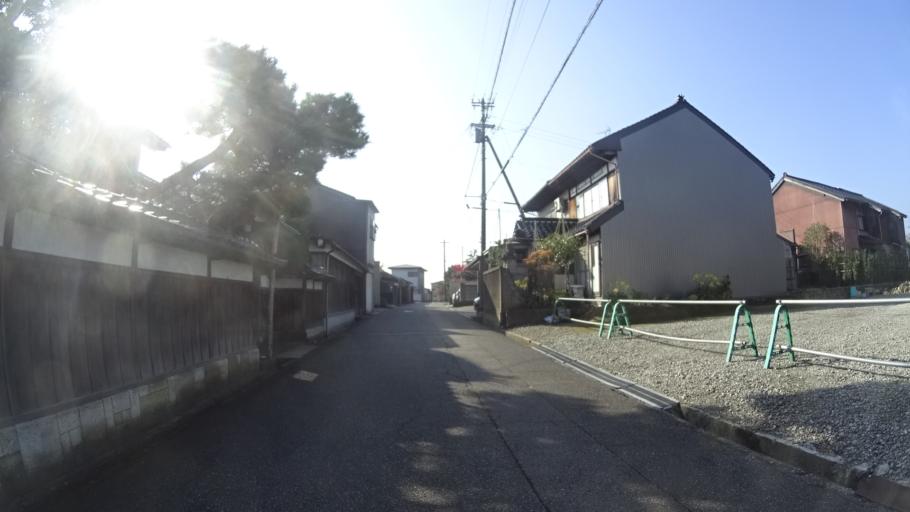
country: JP
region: Toyama
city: Nishishinminato
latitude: 36.7938
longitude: 137.0575
